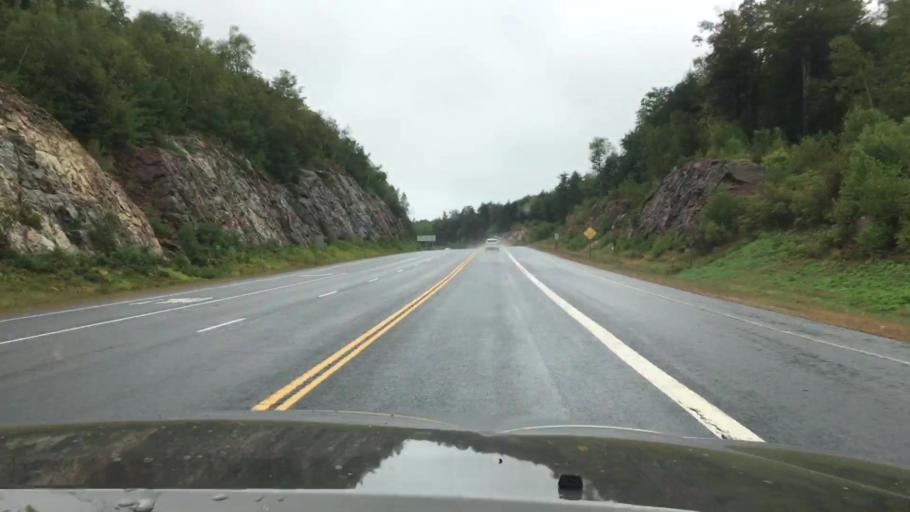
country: US
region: New Hampshire
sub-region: Cheshire County
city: Harrisville
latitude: 43.0065
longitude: -72.1614
